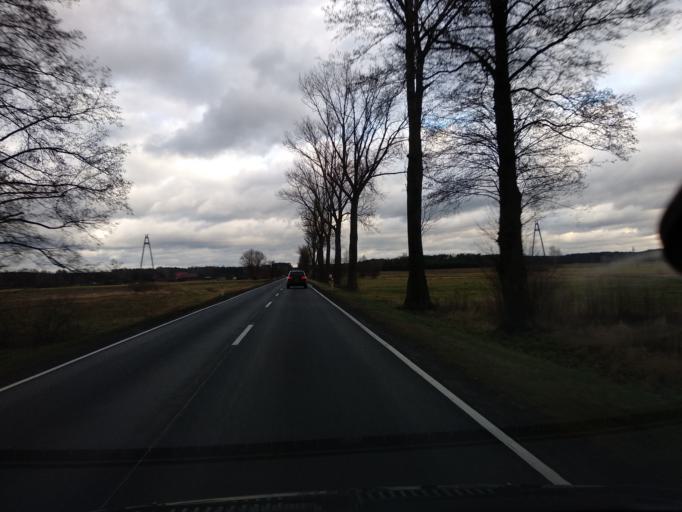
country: PL
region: Greater Poland Voivodeship
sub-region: Powiat ostrowski
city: Jankow Przygodzki
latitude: 51.4897
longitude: 17.7739
